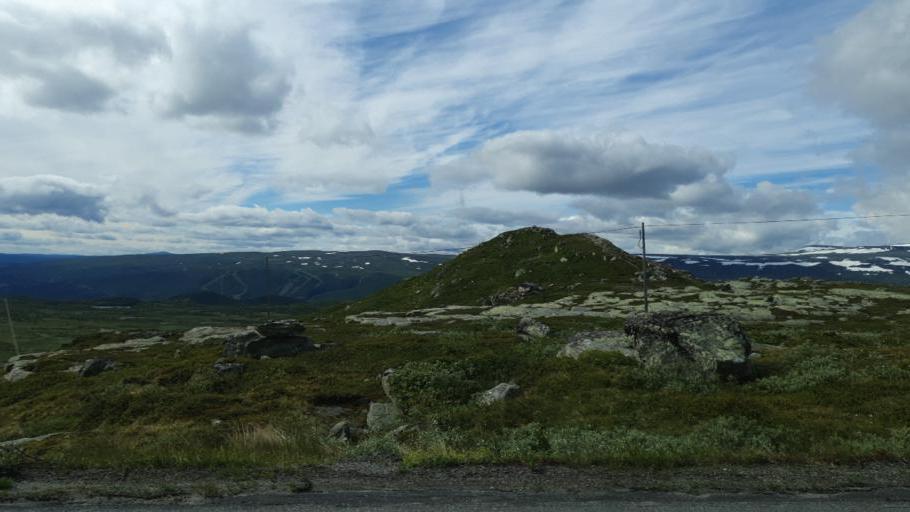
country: NO
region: Oppland
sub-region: Vestre Slidre
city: Slidre
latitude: 61.2826
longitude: 8.8348
